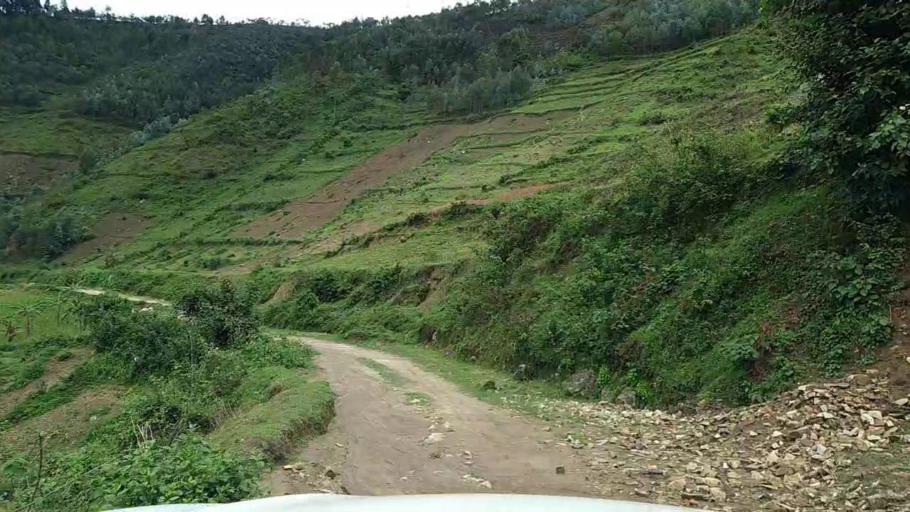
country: RW
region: Southern Province
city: Gikongoro
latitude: -2.3606
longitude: 29.4973
